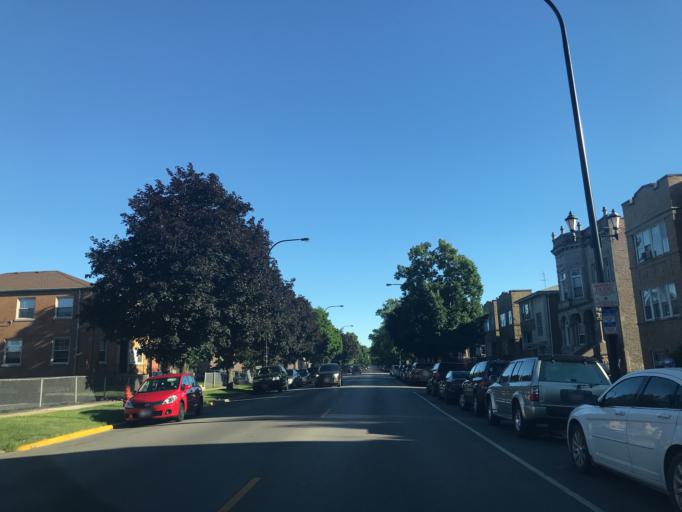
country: US
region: Illinois
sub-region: Cook County
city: Berwyn
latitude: 41.8611
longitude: -87.7740
